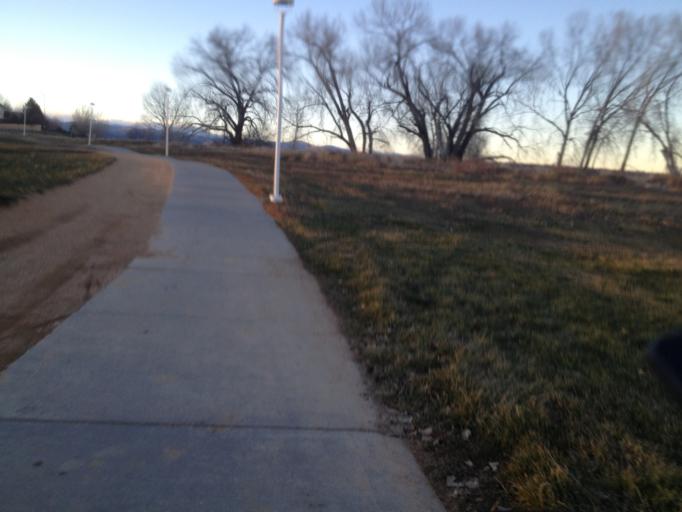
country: US
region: Colorado
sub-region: Boulder County
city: Superior
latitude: 39.9536
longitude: -105.1449
